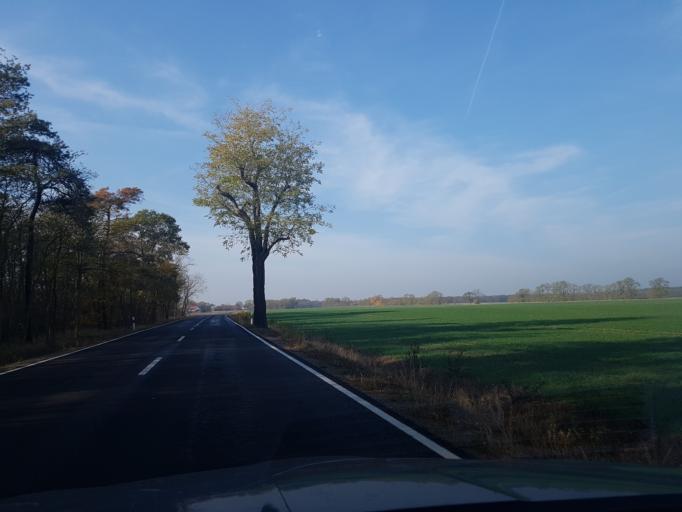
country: DE
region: Saxony
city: Arzberg
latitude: 51.5426
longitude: 13.1822
